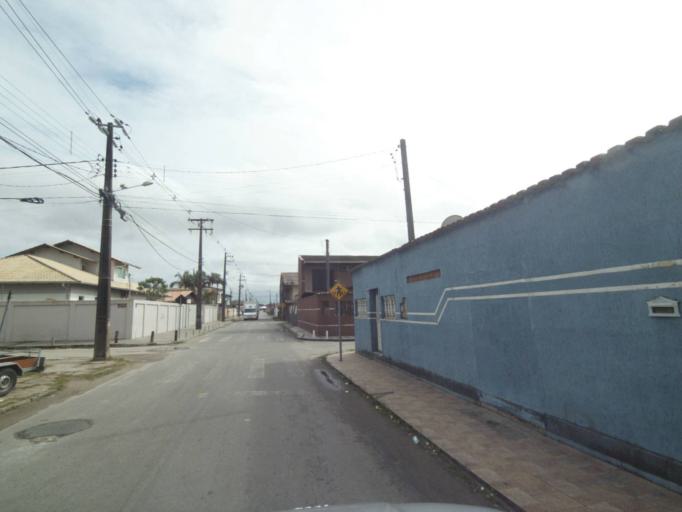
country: BR
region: Parana
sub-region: Paranagua
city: Paranagua
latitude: -25.5667
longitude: -48.5626
